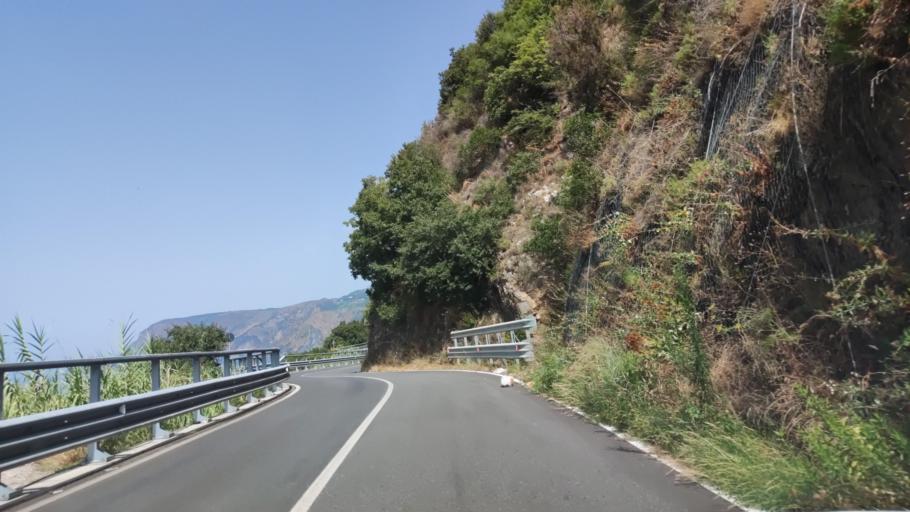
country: IT
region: Calabria
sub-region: Provincia di Reggio Calabria
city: Bagnara Calabra
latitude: 38.2723
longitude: 15.7820
